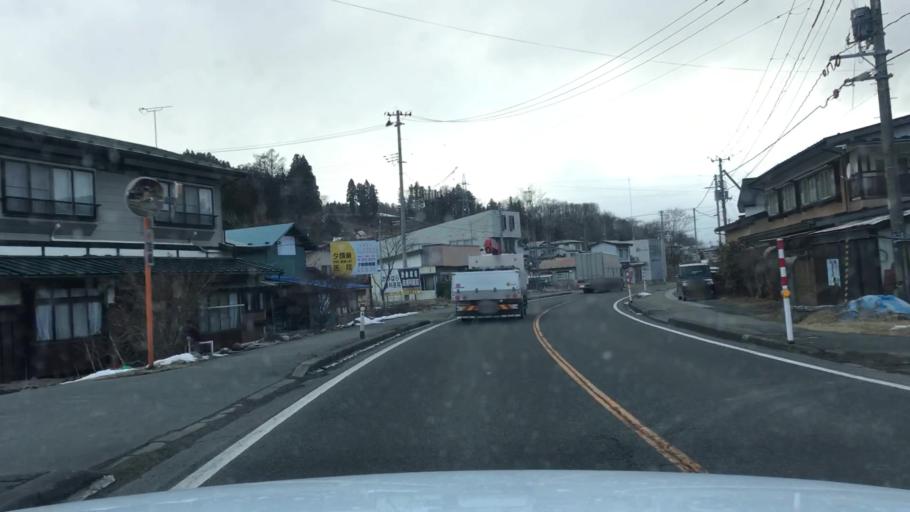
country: JP
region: Iwate
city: Morioka-shi
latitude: 39.6812
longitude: 141.1837
